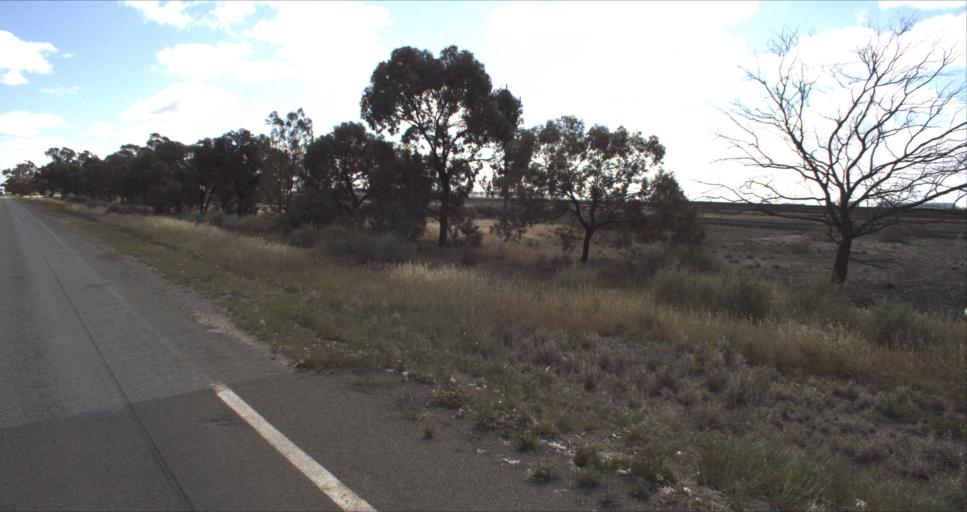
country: AU
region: New South Wales
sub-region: Murrumbidgee Shire
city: Darlington Point
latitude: -34.5739
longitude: 146.1666
